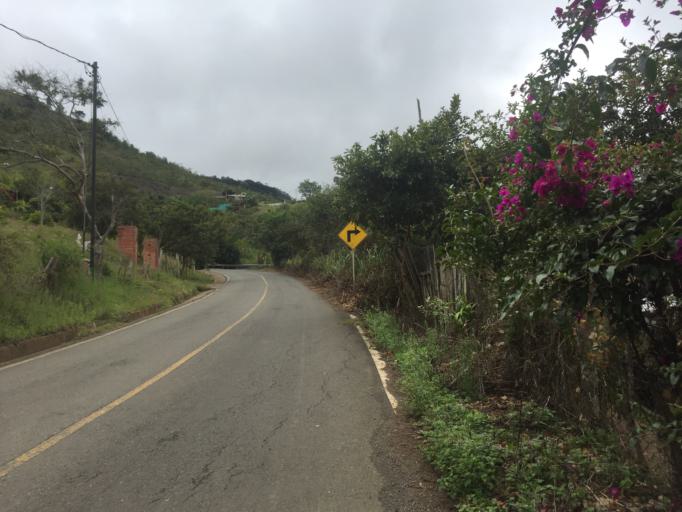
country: CO
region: Valle del Cauca
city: Dagua
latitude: 3.6967
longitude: -76.5889
